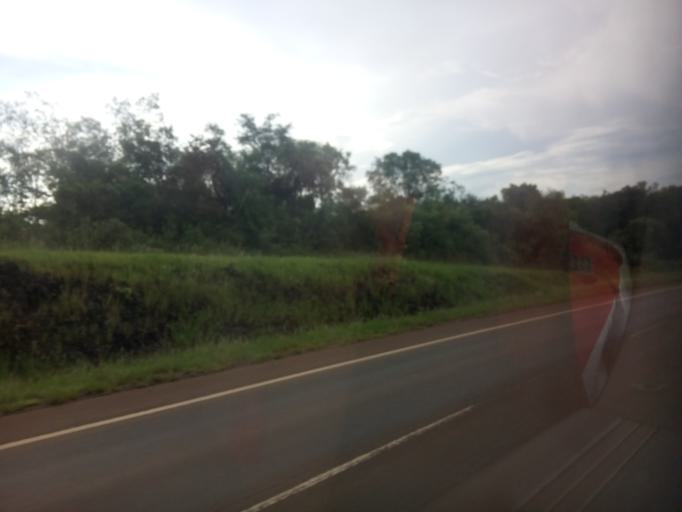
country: AR
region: Misiones
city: Santa Ana
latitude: -27.3990
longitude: -55.6026
